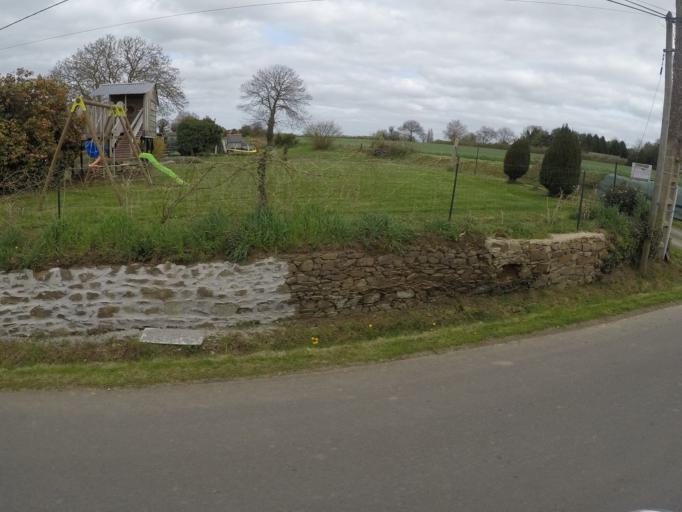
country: FR
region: Brittany
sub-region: Departement des Cotes-d'Armor
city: Plouha
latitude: 48.6642
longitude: -2.9205
